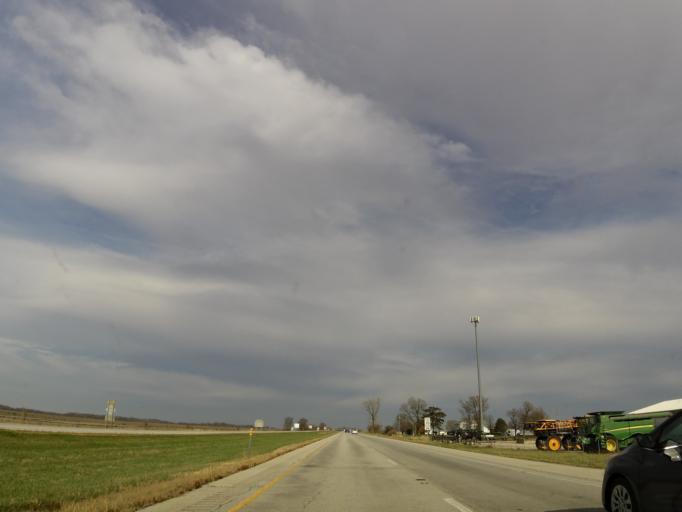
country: US
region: Illinois
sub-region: Knox County
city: Galesburg
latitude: 40.9917
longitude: -90.3359
